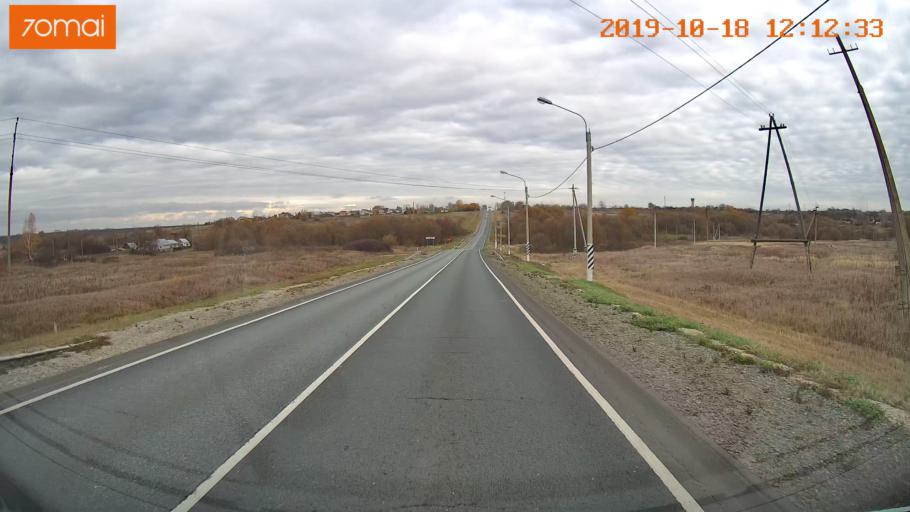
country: RU
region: Rjazan
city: Zakharovo
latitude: 54.4127
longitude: 39.3594
